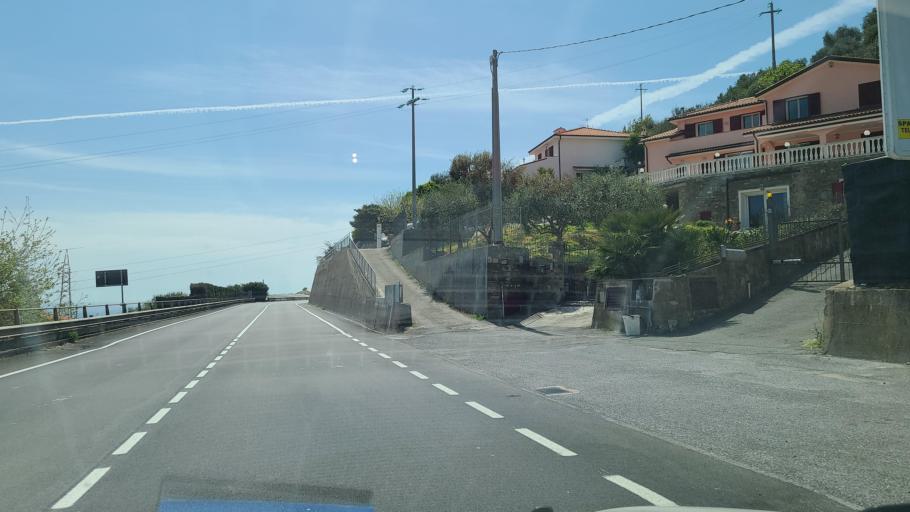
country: IT
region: Liguria
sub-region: Provincia di Imperia
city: Taggia
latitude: 43.8498
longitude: 7.8412
